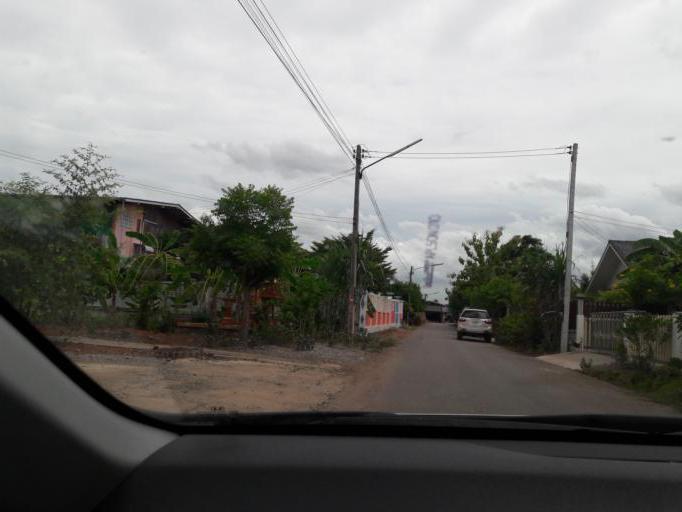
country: TH
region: Ratchaburi
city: Damnoen Saduak
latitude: 13.5432
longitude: 100.0032
